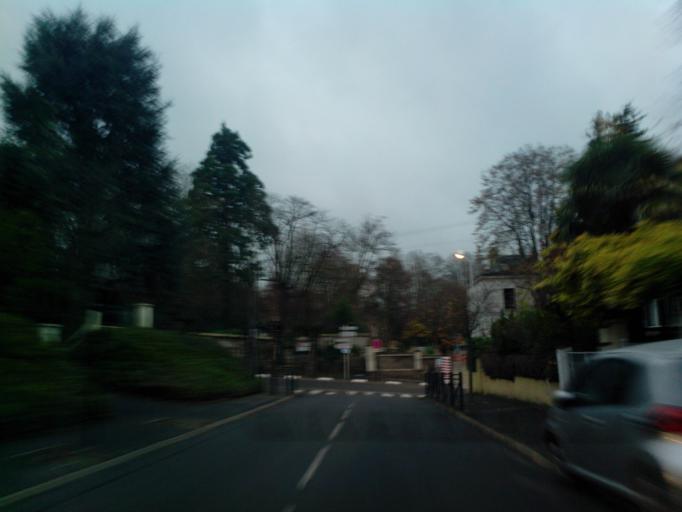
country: FR
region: Ile-de-France
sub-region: Departement de l'Essonne
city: Evry
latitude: 48.6341
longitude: 2.4516
